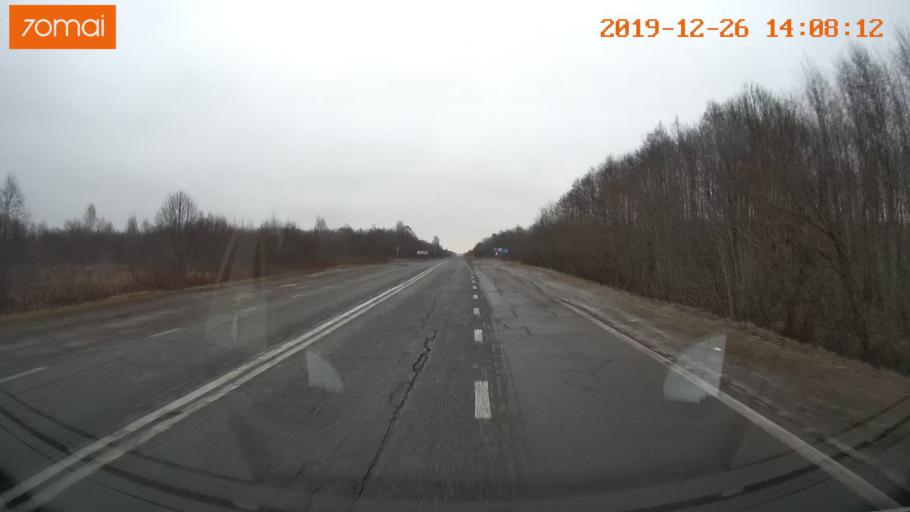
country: RU
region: Jaroslavl
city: Poshekhon'ye
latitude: 58.5087
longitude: 38.9073
